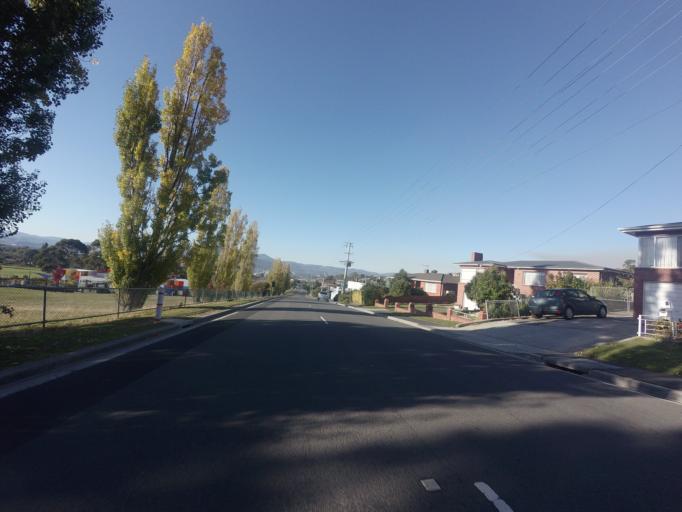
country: AU
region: Tasmania
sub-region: Glenorchy
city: West Moonah
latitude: -42.8501
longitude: 147.2576
